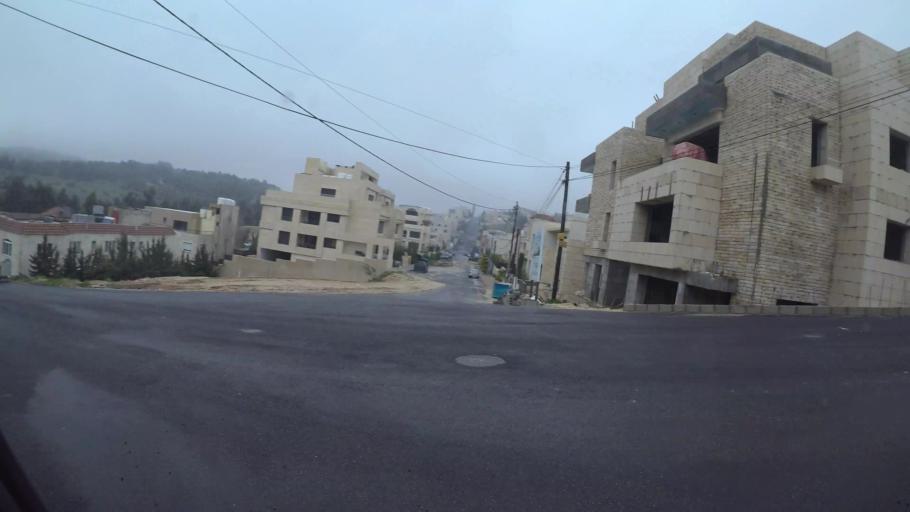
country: JO
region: Amman
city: Wadi as Sir
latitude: 32.0014
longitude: 35.8191
